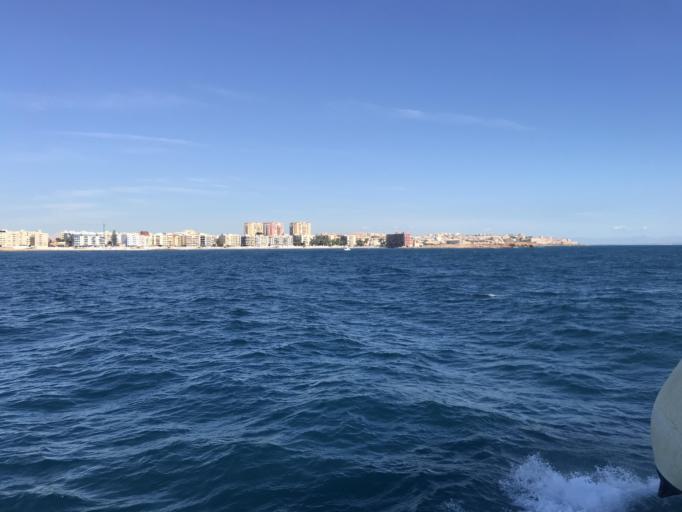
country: ES
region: Valencia
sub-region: Provincia de Alicante
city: Torrevieja
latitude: 37.9749
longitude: -0.6574
